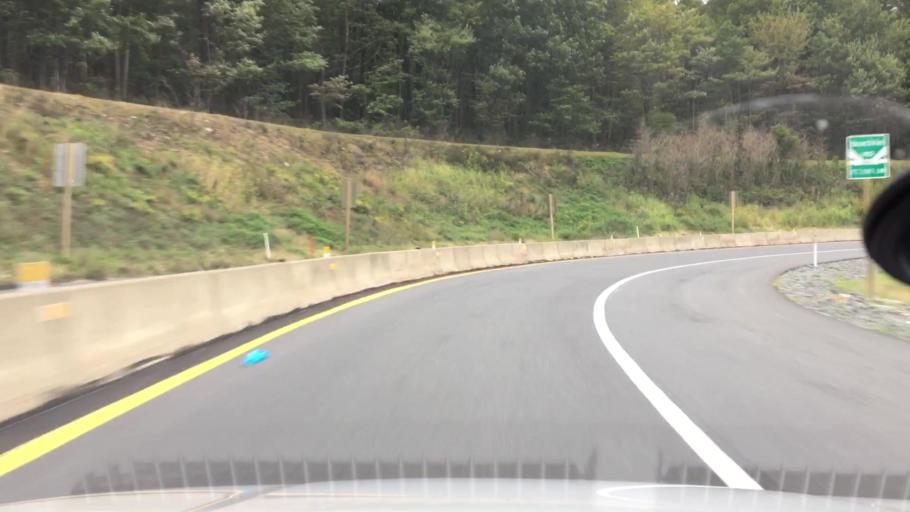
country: US
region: Pennsylvania
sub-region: Luzerne County
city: White Haven
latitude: 41.0742
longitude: -75.7061
